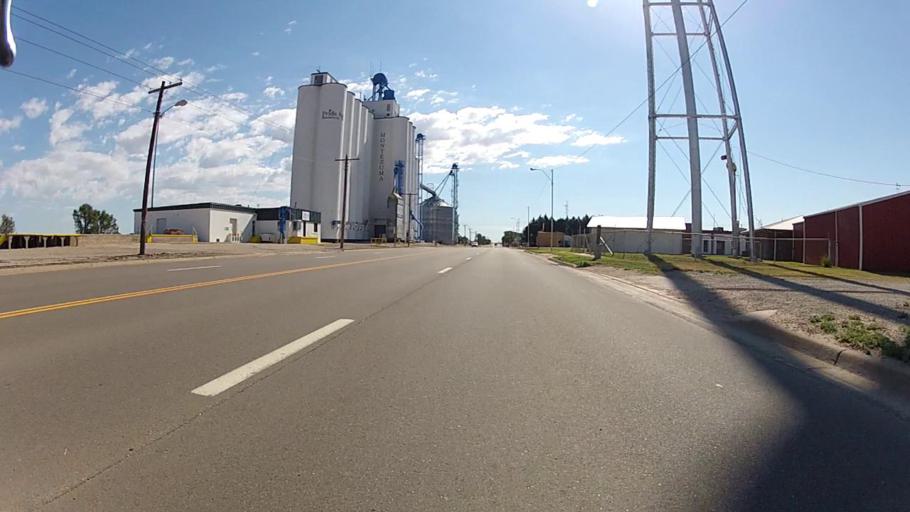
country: US
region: Kansas
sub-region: Gray County
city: Cimarron
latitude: 37.5985
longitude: -100.4449
